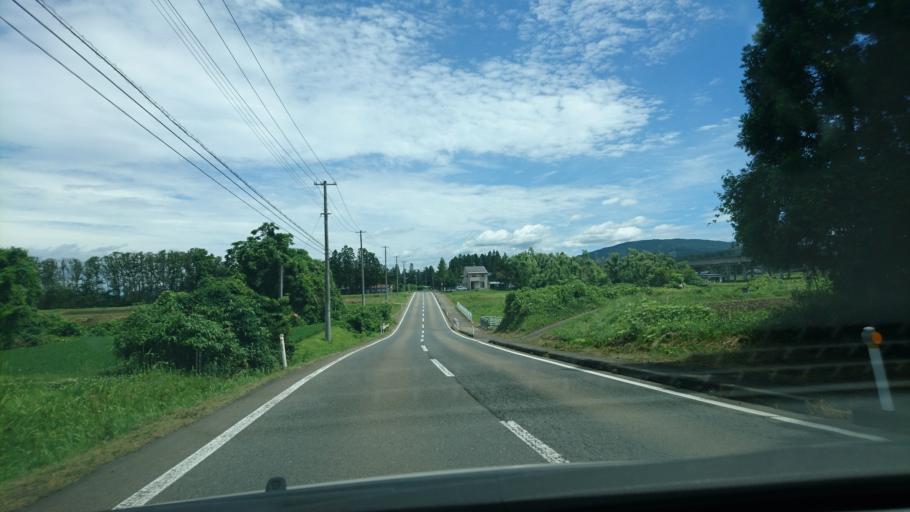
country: JP
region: Iwate
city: Hanamaki
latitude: 39.4185
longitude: 141.1744
